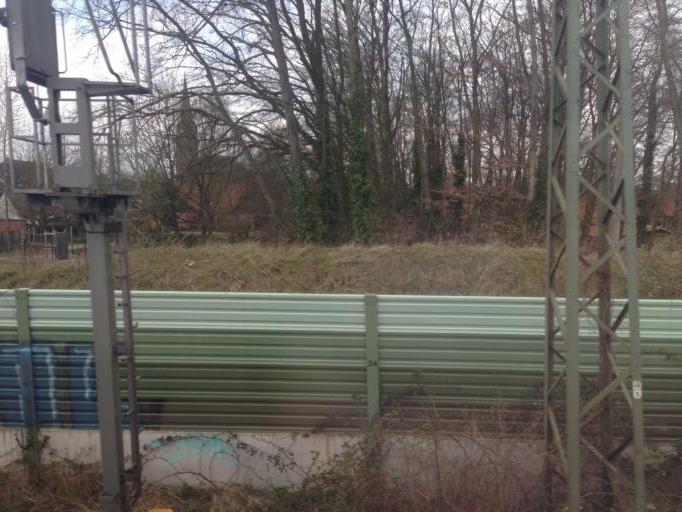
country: DE
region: North Rhine-Westphalia
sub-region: Regierungsbezirk Munster
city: Nottuln
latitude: 51.8633
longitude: 7.3717
